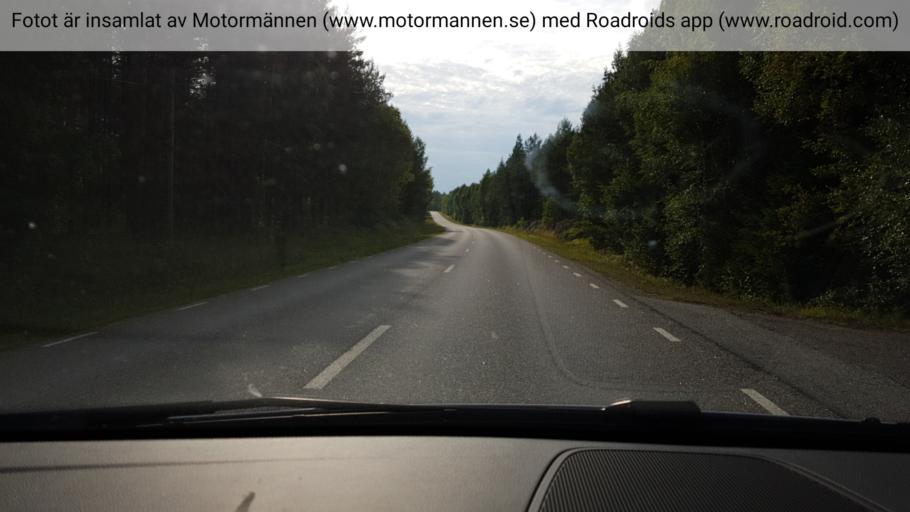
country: SE
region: Stockholm
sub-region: Norrtalje Kommun
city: Nykvarn
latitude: 59.9071
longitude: 18.3192
